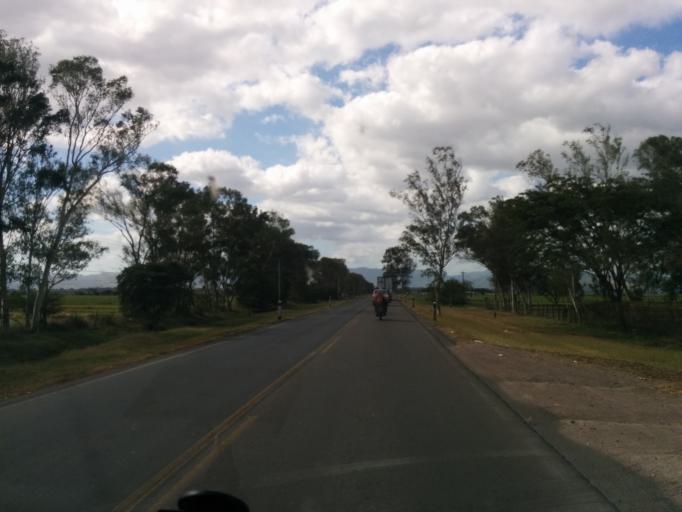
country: NI
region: Matagalpa
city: Ciudad Dario
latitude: 12.8645
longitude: -86.1137
